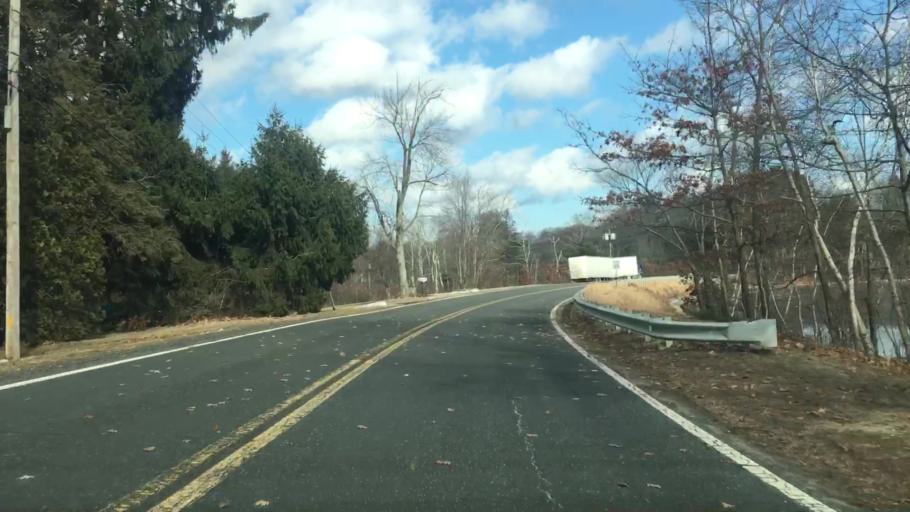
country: US
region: Massachusetts
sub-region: Hampden County
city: Wales
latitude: 42.0625
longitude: -72.2255
